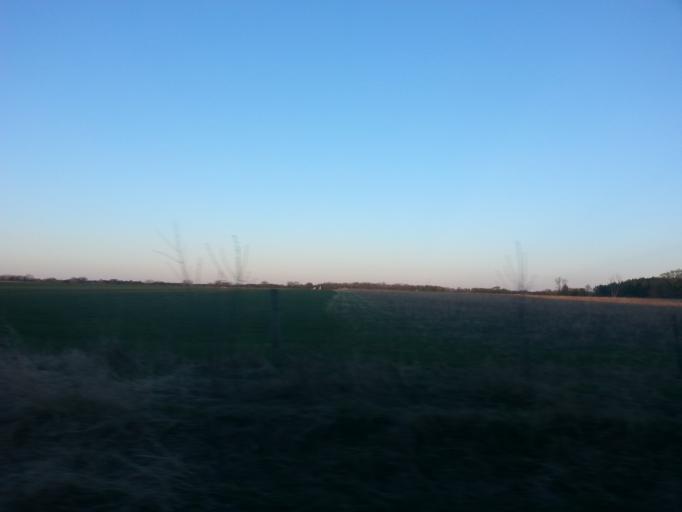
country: US
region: Minnesota
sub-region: Washington County
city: Lakeland
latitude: 44.9456
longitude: -92.7971
